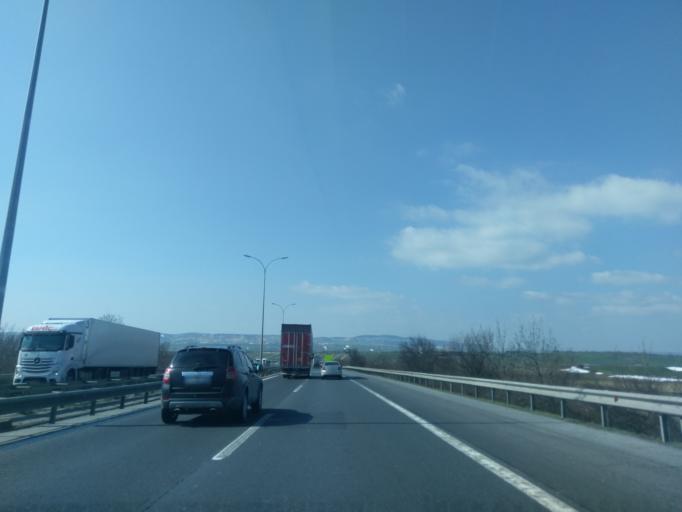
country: TR
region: Istanbul
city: Tepecik
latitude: 41.1068
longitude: 28.5785
